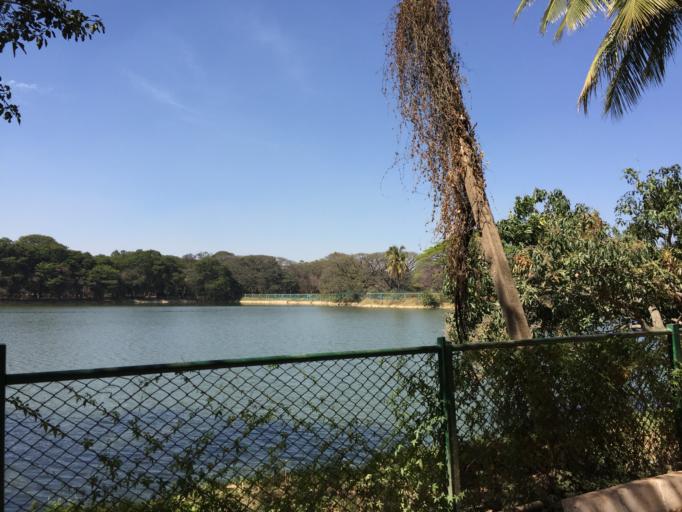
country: IN
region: Karnataka
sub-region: Bangalore Urban
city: Bangalore
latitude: 12.9446
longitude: 77.5836
